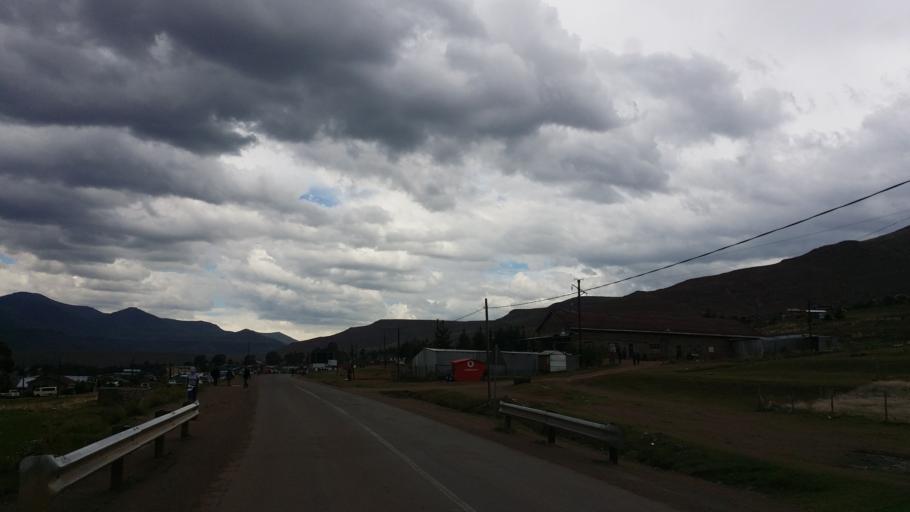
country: LS
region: Mokhotlong
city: Mokhotlong
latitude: -29.2884
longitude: 29.0534
